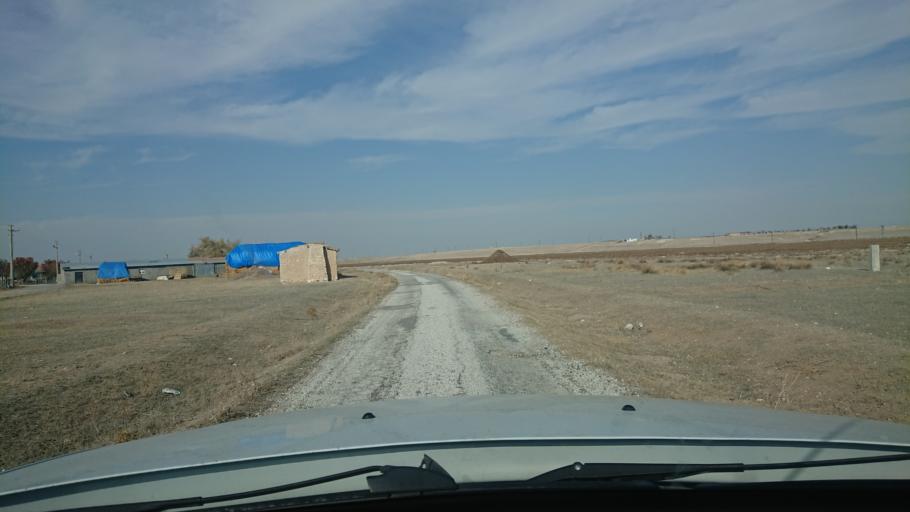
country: TR
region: Aksaray
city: Sultanhani
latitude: 38.2587
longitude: 33.4745
